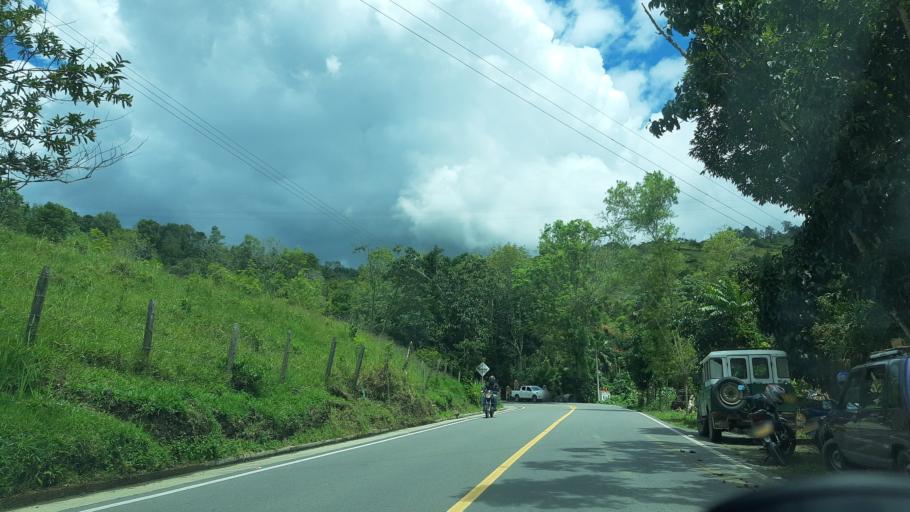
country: CO
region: Boyaca
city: Guateque
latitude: 5.0115
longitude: -73.4541
